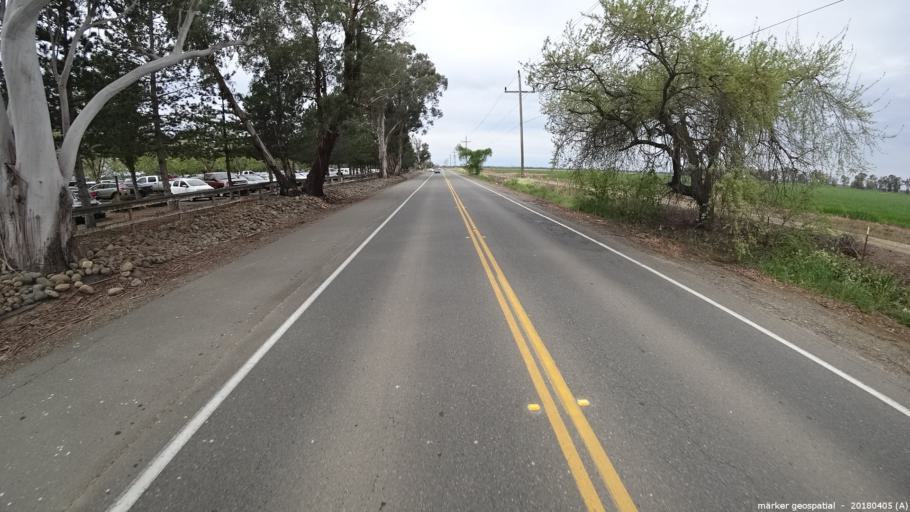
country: US
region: California
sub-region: Sacramento County
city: Galt
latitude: 38.2910
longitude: -121.3285
